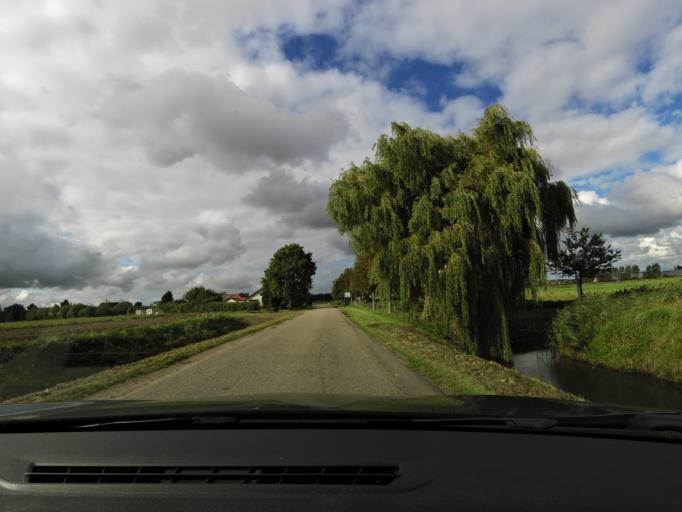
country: NL
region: South Holland
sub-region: Gemeente Brielle
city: Brielle
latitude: 51.8854
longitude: 4.1728
